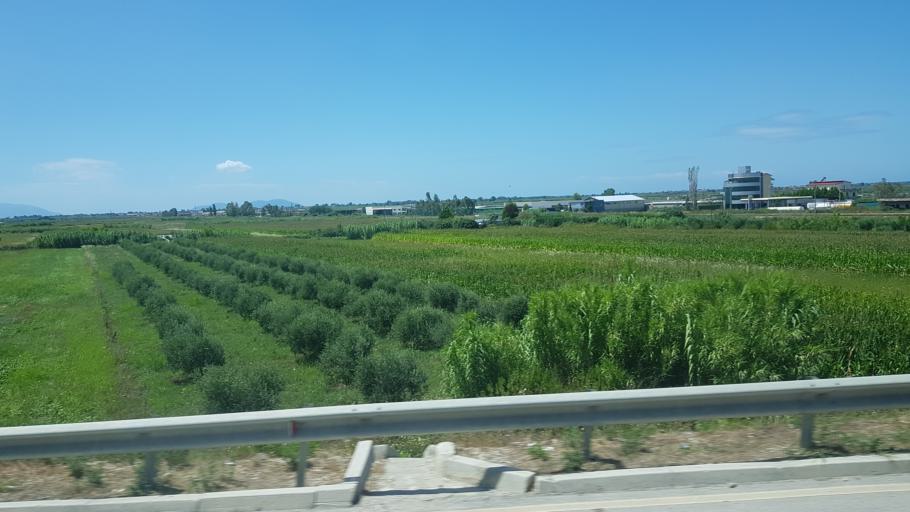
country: AL
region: Fier
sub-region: Rrethi i Fierit
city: Levan
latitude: 40.6678
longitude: 19.4864
